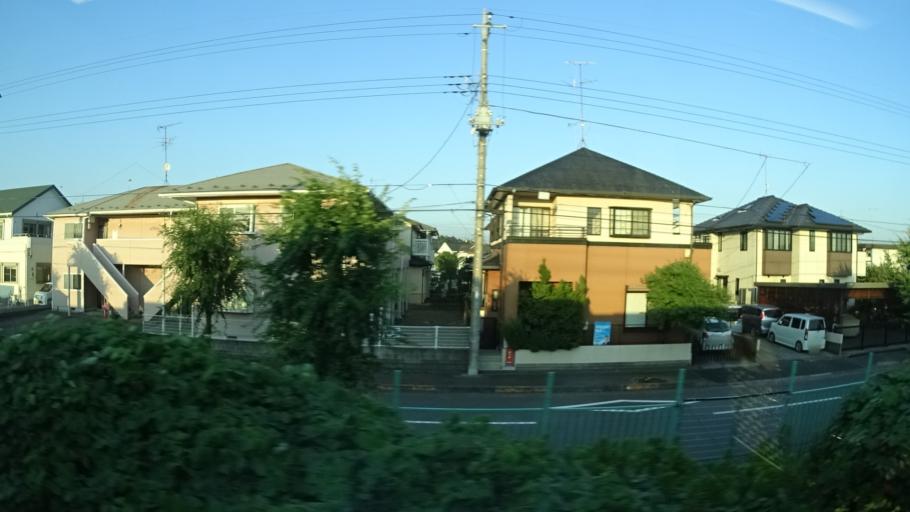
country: JP
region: Ibaraki
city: Fujishiro
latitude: 35.9347
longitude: 140.1384
